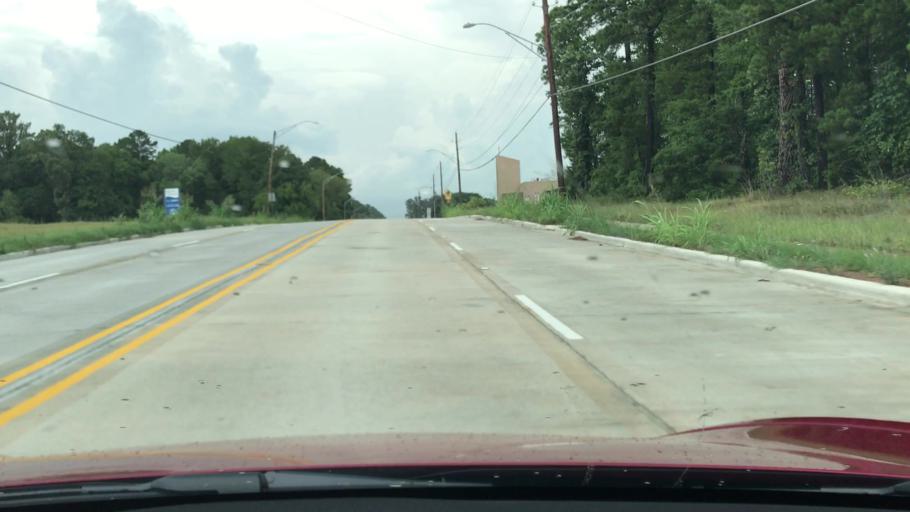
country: US
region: Louisiana
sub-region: Bossier Parish
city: Bossier City
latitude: 32.4012
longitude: -93.7633
